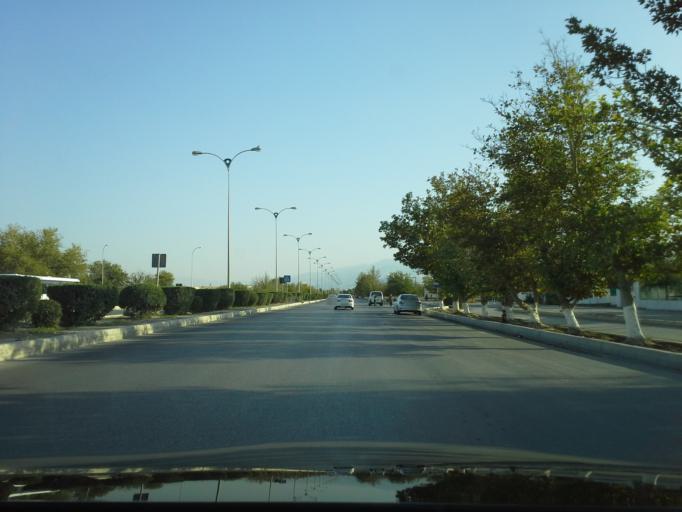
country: TM
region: Ahal
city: Abadan
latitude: 38.0409
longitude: 58.1863
